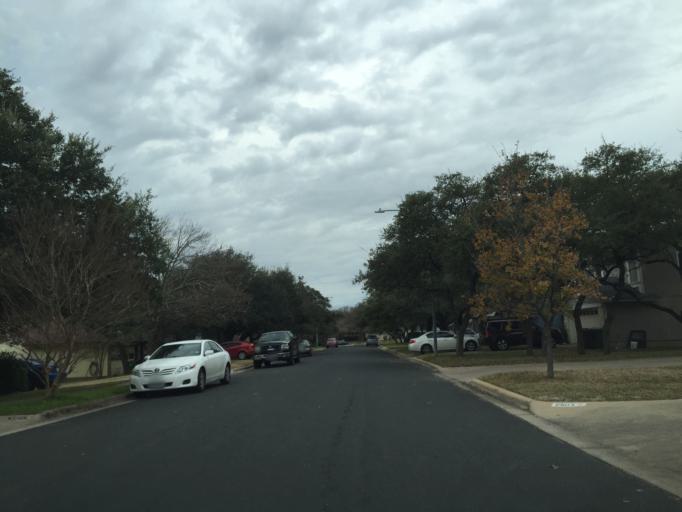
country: US
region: Texas
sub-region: Williamson County
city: Jollyville
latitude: 30.4488
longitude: -97.7471
